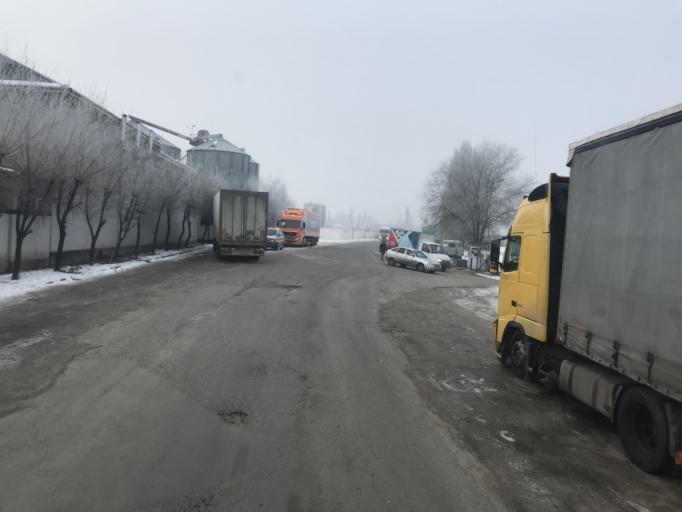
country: KZ
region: Almaty Oblysy
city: Pervomayskiy
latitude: 43.3611
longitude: 76.9776
